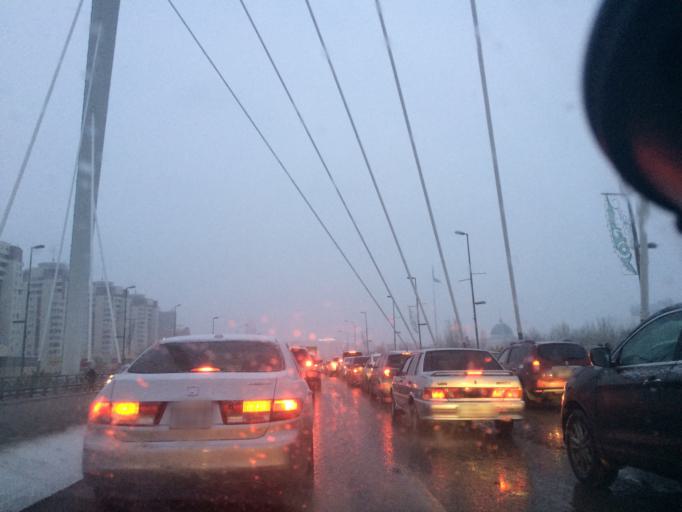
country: KZ
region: Astana Qalasy
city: Astana
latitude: 51.1520
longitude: 71.4283
